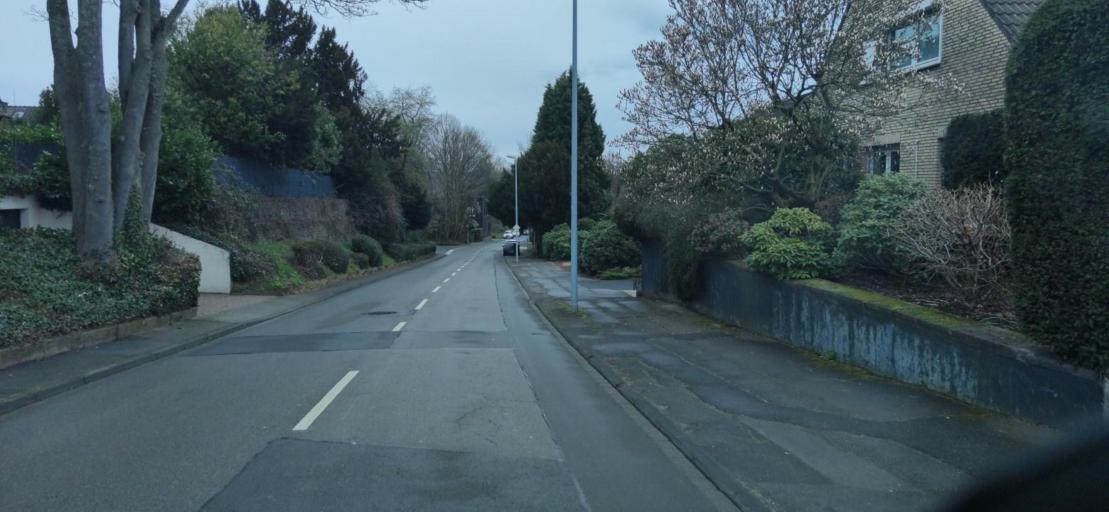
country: DE
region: North Rhine-Westphalia
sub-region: Regierungsbezirk Dusseldorf
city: Muelheim (Ruhr)
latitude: 51.4197
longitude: 6.9114
